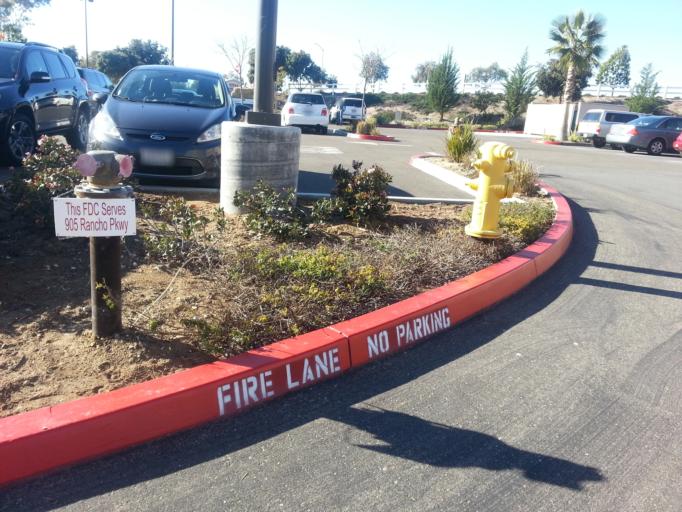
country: US
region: California
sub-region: San Luis Obispo County
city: Arroyo Grande
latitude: 35.1269
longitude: -120.5933
